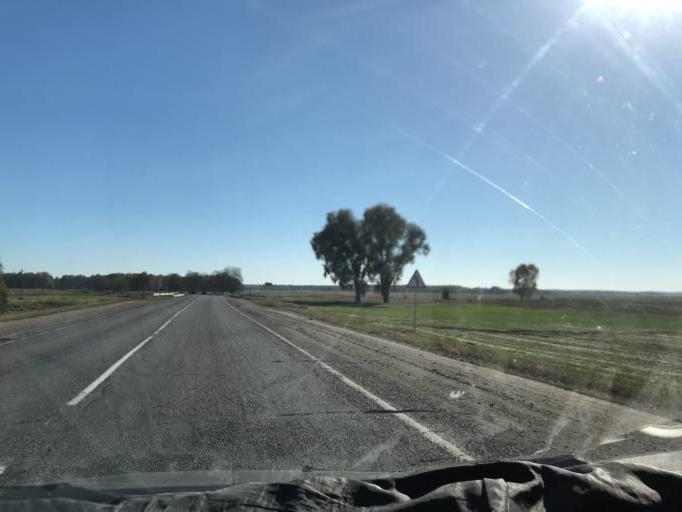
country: BY
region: Gomel
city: Kalinkavichy
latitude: 52.3905
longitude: 29.3132
